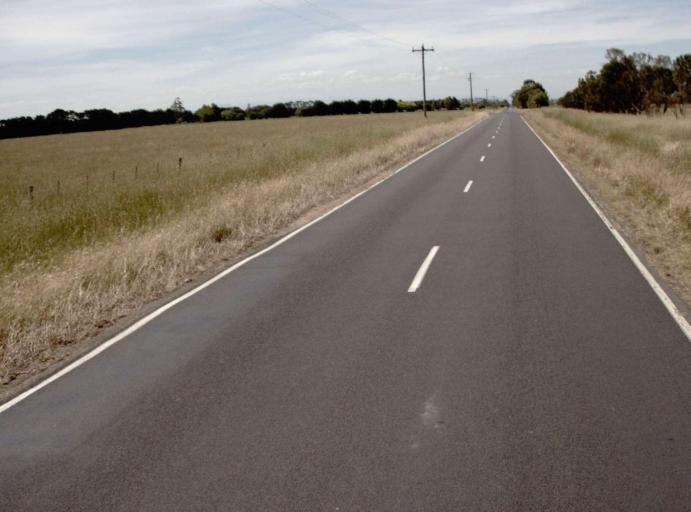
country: AU
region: Victoria
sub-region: Wellington
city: Heyfield
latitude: -38.1040
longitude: 146.8636
